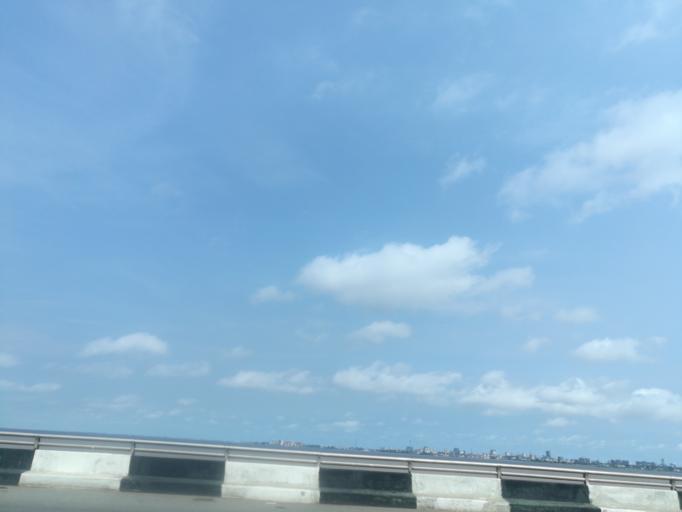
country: NG
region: Lagos
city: Makoko
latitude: 6.4908
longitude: 3.3979
